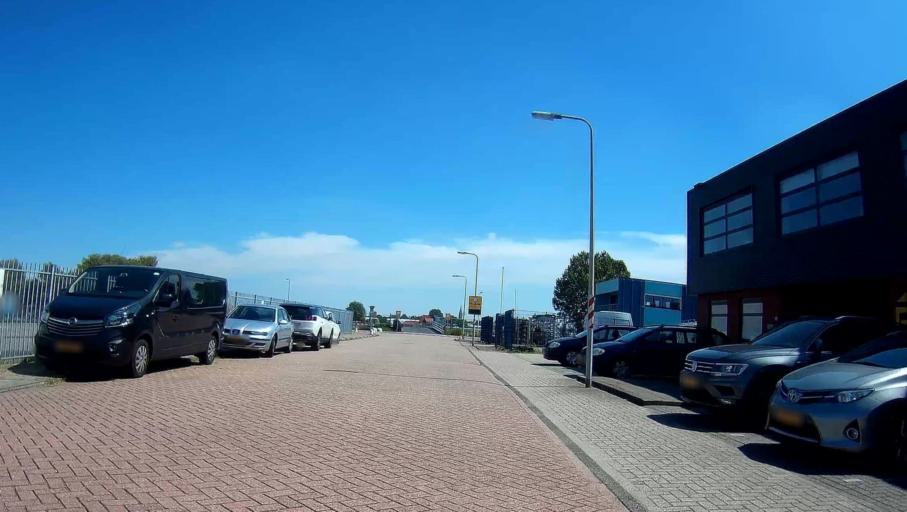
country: NL
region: South Holland
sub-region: Gemeente Westland
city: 's-Gravenzande
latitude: 51.9948
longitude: 4.1814
